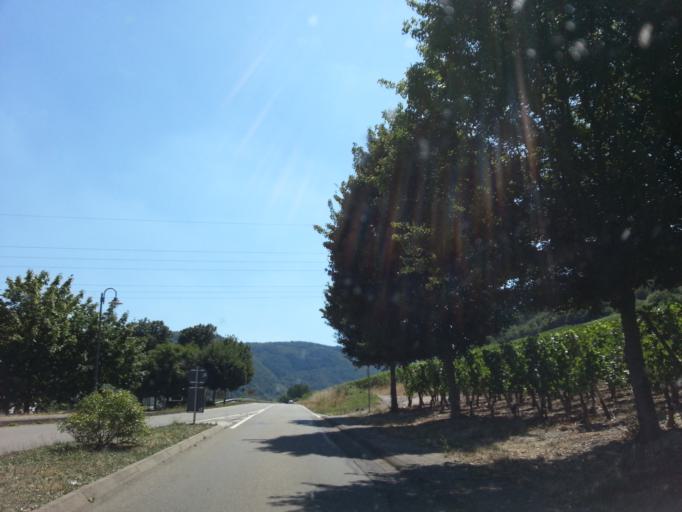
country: DE
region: Rheinland-Pfalz
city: Schleich
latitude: 49.8110
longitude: 6.8414
